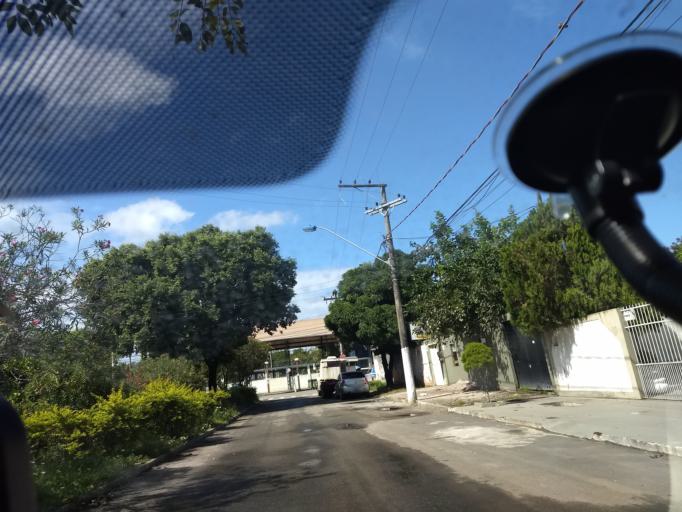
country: BR
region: Espirito Santo
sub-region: Vitoria
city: Vitoria
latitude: -20.3543
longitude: -40.3568
